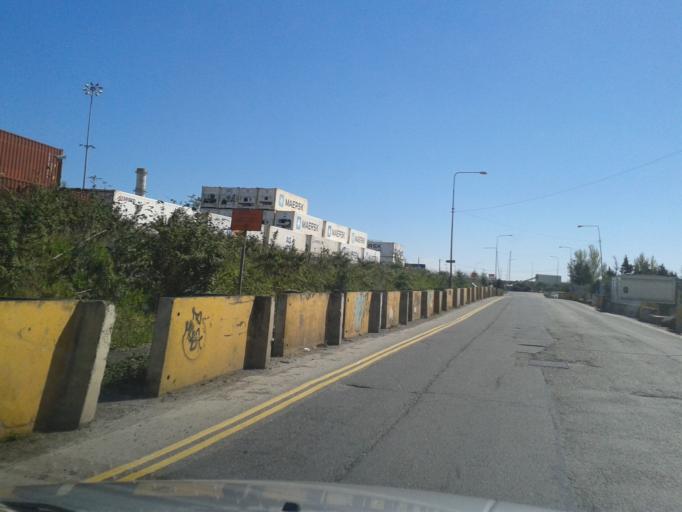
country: IE
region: Leinster
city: Sandymount
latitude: 53.3408
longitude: -6.2121
